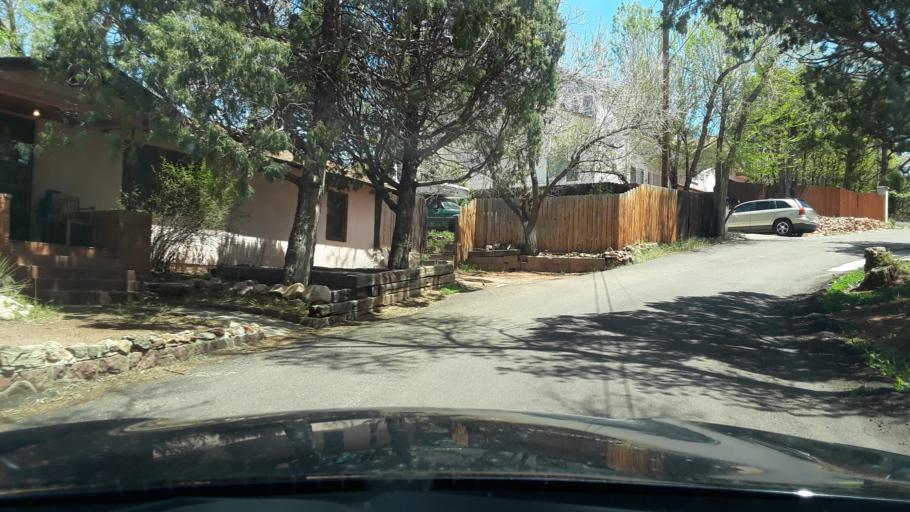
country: US
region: Colorado
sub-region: El Paso County
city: Manitou Springs
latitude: 38.8613
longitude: -104.8839
